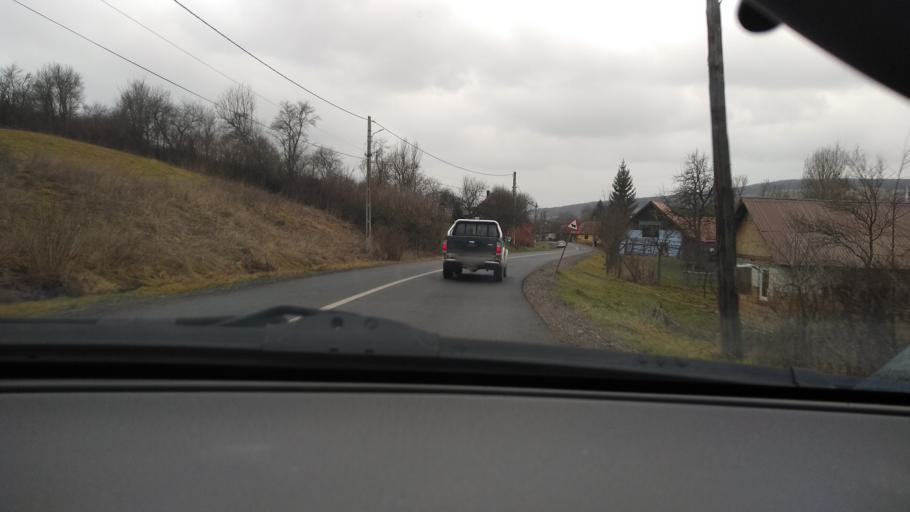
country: RO
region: Mures
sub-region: Comuna Bereni
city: Bereni
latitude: 46.5579
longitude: 24.8716
